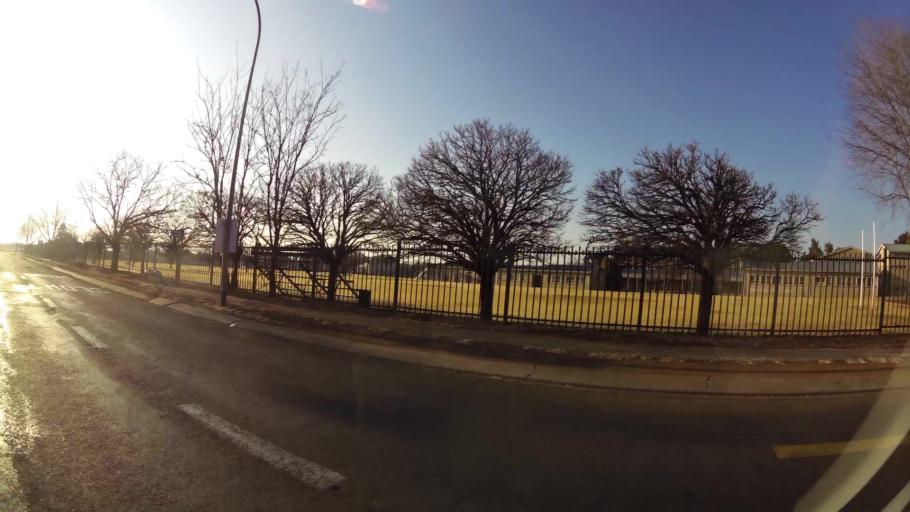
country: ZA
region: Orange Free State
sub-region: Mangaung Metropolitan Municipality
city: Bloemfontein
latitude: -29.1465
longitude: 26.1673
